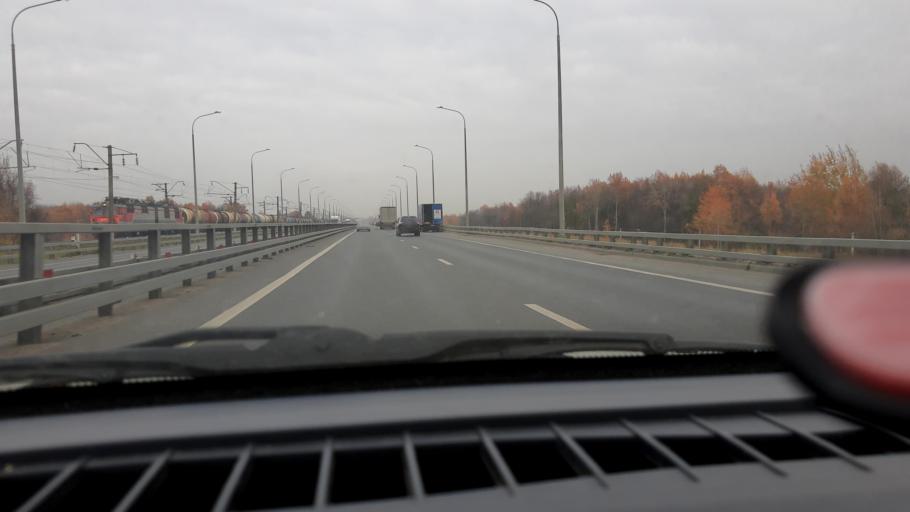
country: RU
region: Nizjnij Novgorod
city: Neklyudovo
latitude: 56.3823
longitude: 43.9640
